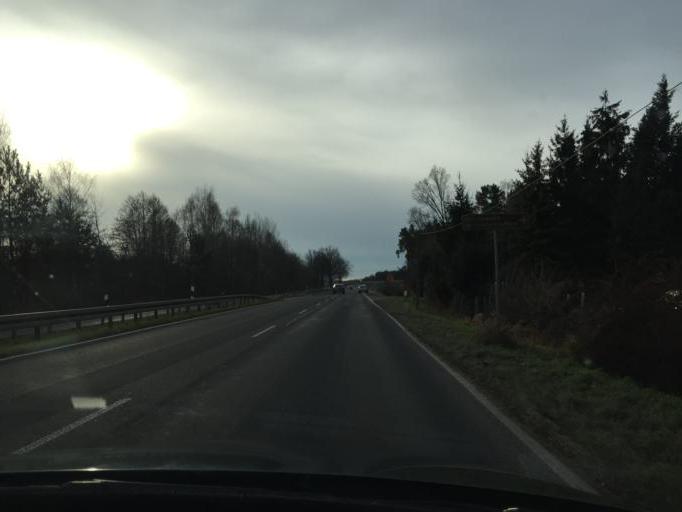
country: DE
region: Brandenburg
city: Cottbus
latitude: 51.7928
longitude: 14.3779
